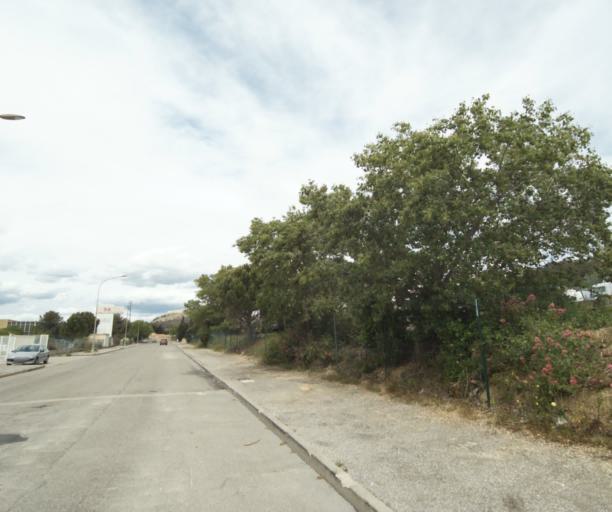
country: FR
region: Provence-Alpes-Cote d'Azur
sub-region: Departement des Bouches-du-Rhone
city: Rognac
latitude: 43.4779
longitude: 5.2370
